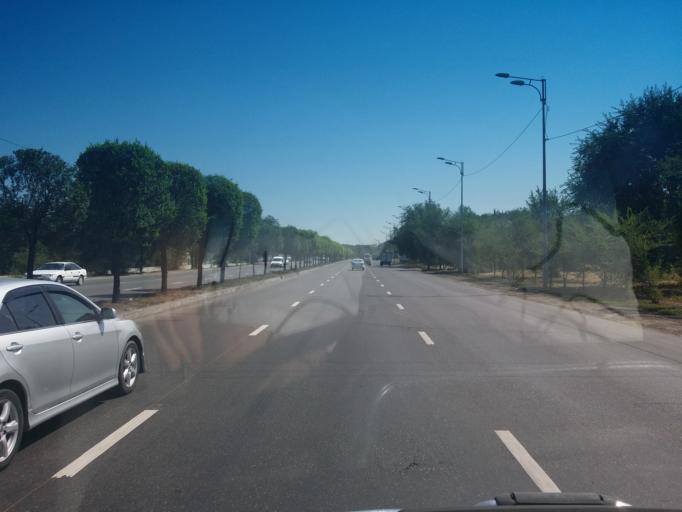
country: KZ
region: Almaty Qalasy
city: Almaty
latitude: 43.2958
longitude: 76.9833
